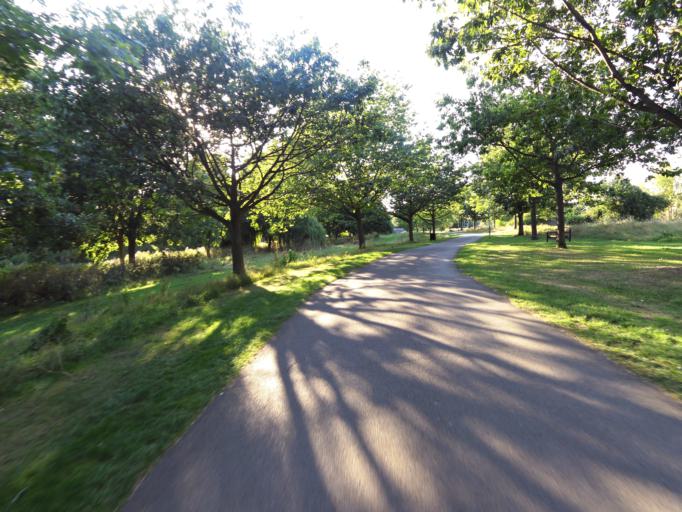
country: GB
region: England
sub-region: Essex
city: Chelmsford
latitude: 51.7331
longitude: 0.4605
